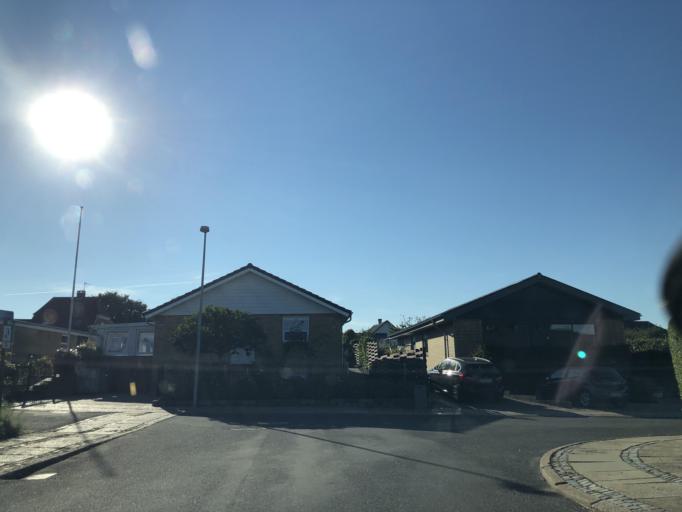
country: DK
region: North Denmark
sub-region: Mariagerfjord Kommune
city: Hobro
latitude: 56.6319
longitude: 9.8039
